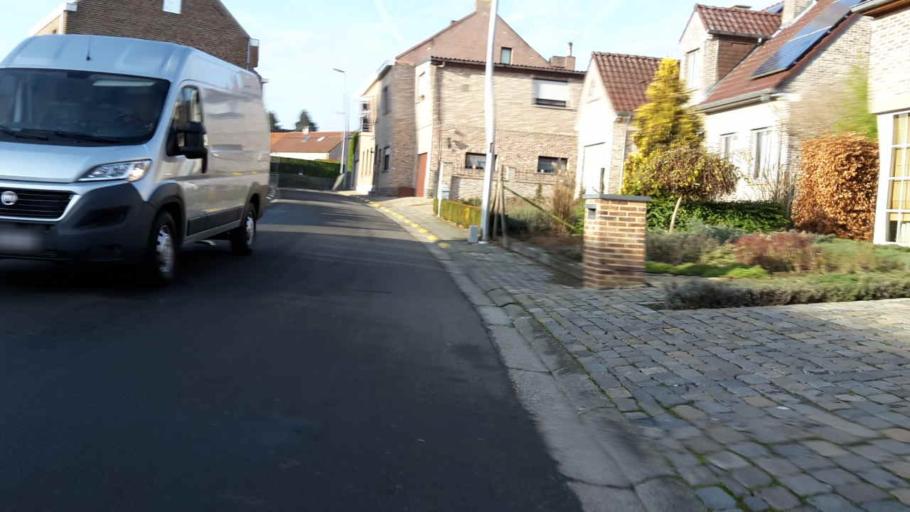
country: BE
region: Flanders
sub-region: Provincie Vlaams-Brabant
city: Hoegaarden
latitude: 50.8184
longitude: 4.8900
